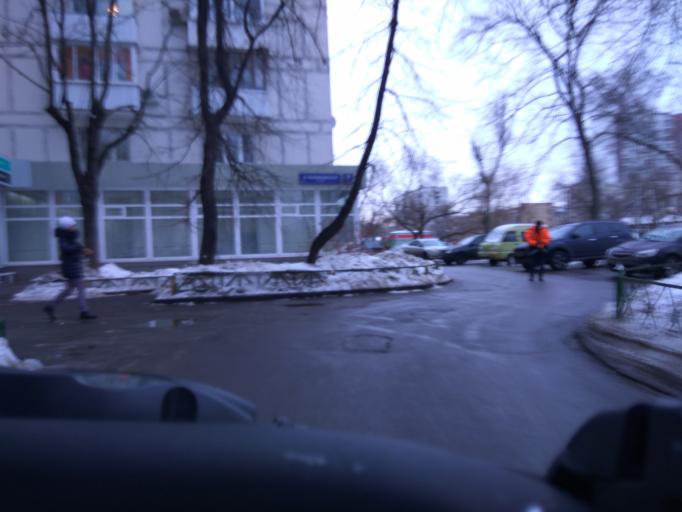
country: RU
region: Moskovskaya
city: Bogorodskoye
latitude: 55.7956
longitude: 37.7158
